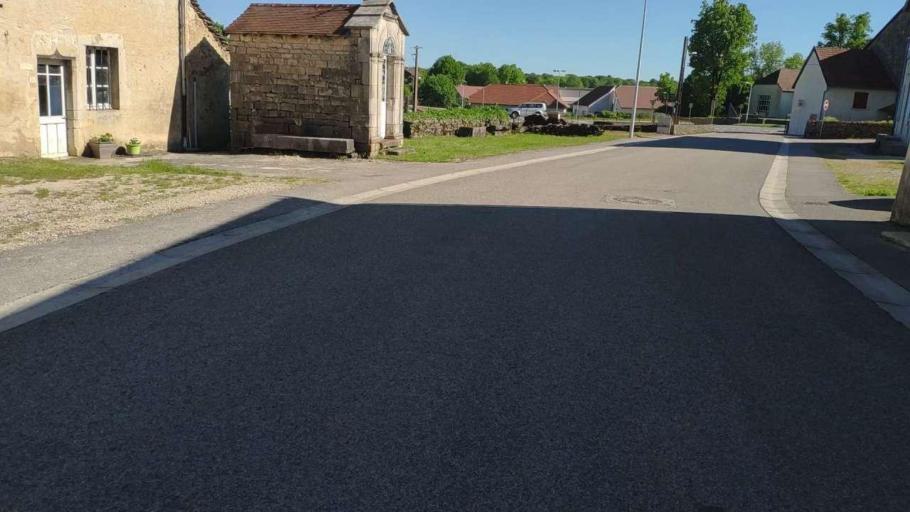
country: FR
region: Franche-Comte
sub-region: Departement du Jura
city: Perrigny
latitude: 46.6873
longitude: 5.6584
